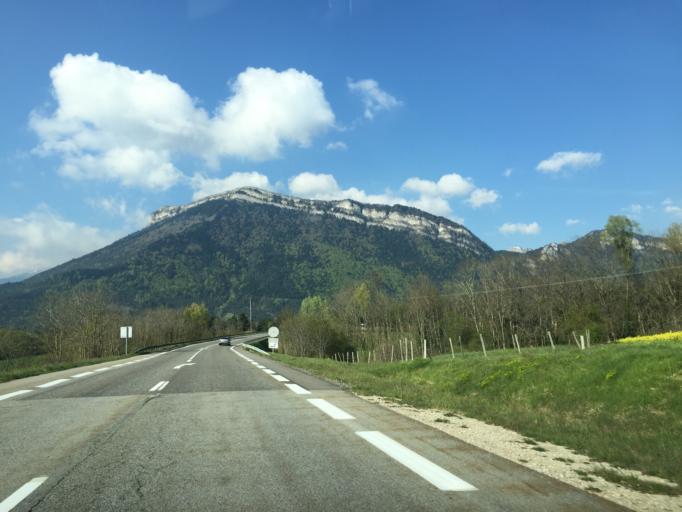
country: FR
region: Rhone-Alpes
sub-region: Departement de l'Isere
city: La Motte-Saint-Martin
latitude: 44.8686
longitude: 5.6183
